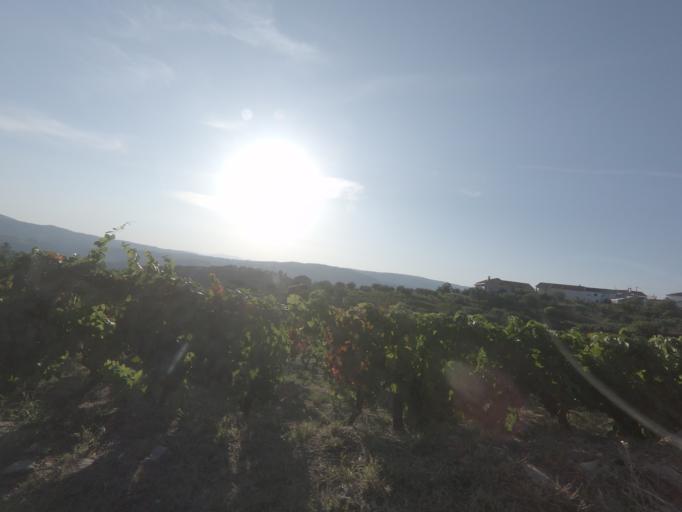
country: PT
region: Vila Real
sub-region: Sabrosa
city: Sabrosa
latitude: 41.2692
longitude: -7.5298
